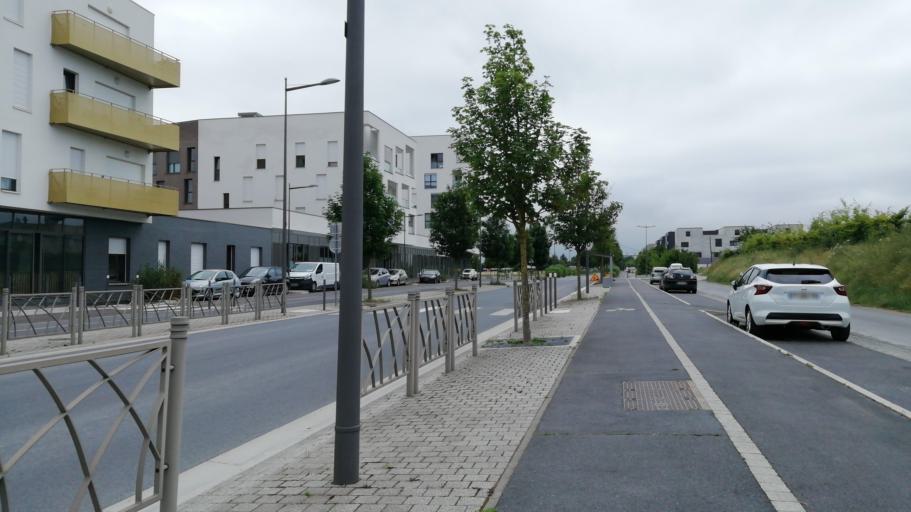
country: FR
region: Champagne-Ardenne
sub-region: Departement de la Marne
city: Betheny
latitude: 49.2628
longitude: 4.0613
